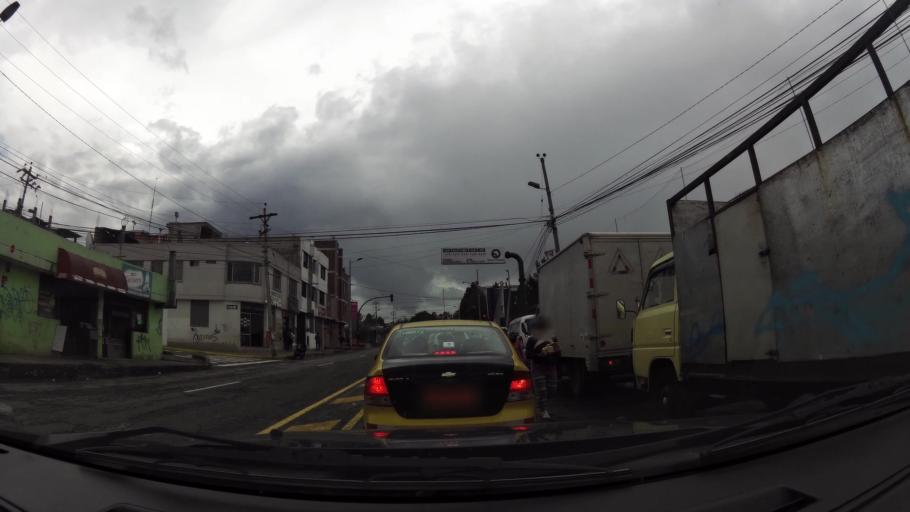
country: EC
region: Pichincha
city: Quito
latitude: -0.2803
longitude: -78.5485
